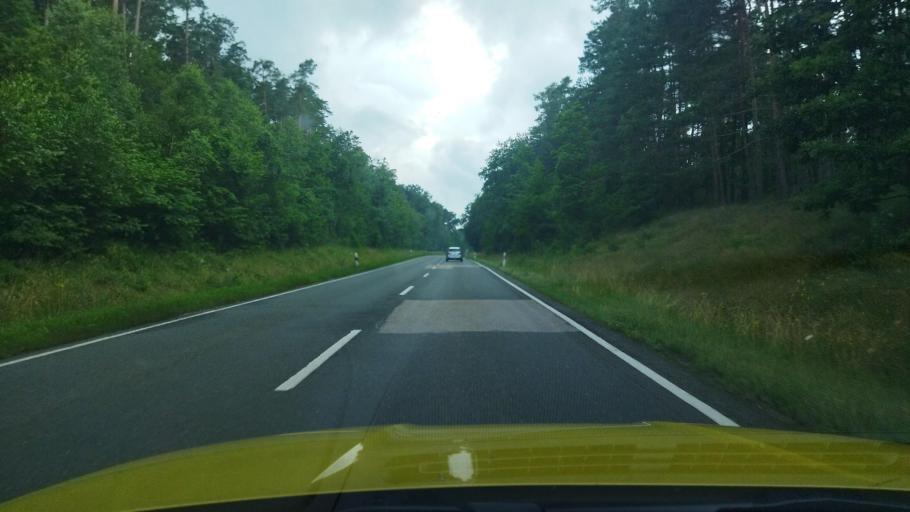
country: DE
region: Bavaria
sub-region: Regierungsbezirk Mittelfranken
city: Pfofeld
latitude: 49.1139
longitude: 10.8660
